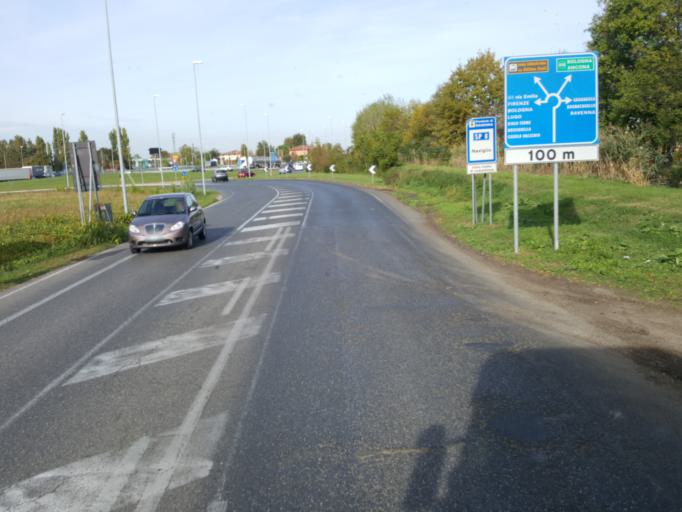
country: IT
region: Emilia-Romagna
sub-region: Provincia di Ravenna
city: Faenza
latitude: 44.3183
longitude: 11.9030
